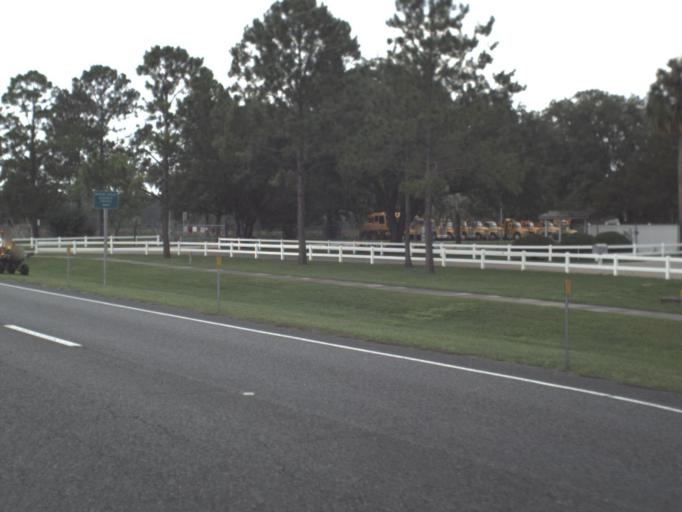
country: US
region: Florida
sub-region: Levy County
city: Chiefland
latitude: 29.4755
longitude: -82.8443
